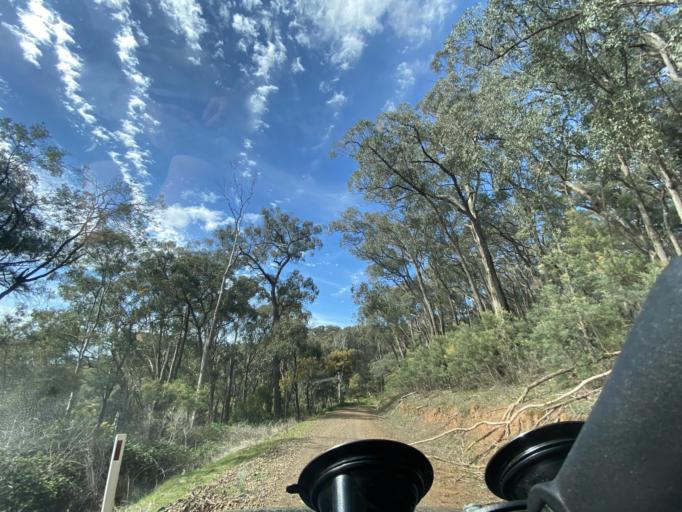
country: AU
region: Victoria
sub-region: Mansfield
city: Mansfield
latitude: -36.8164
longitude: 146.1019
